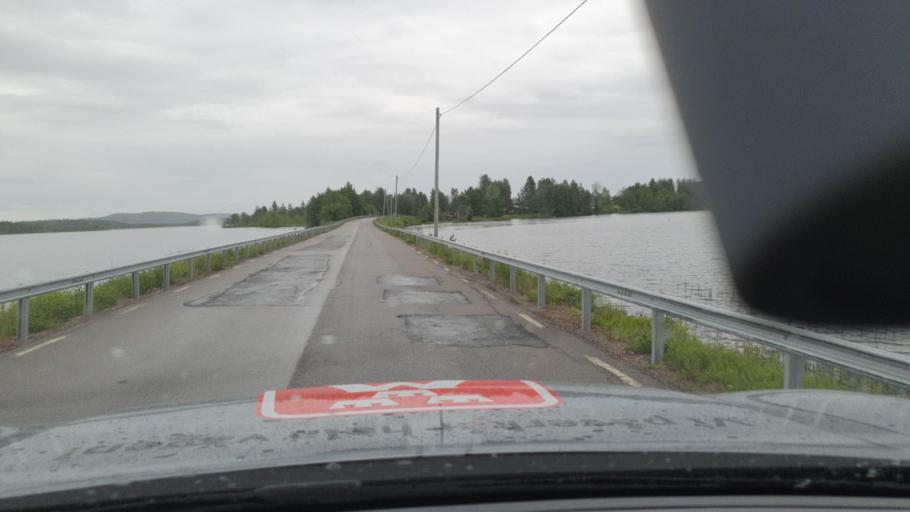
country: SE
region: Norrbotten
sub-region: Pajala Kommun
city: Pajala
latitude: 66.8021
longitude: 23.1216
